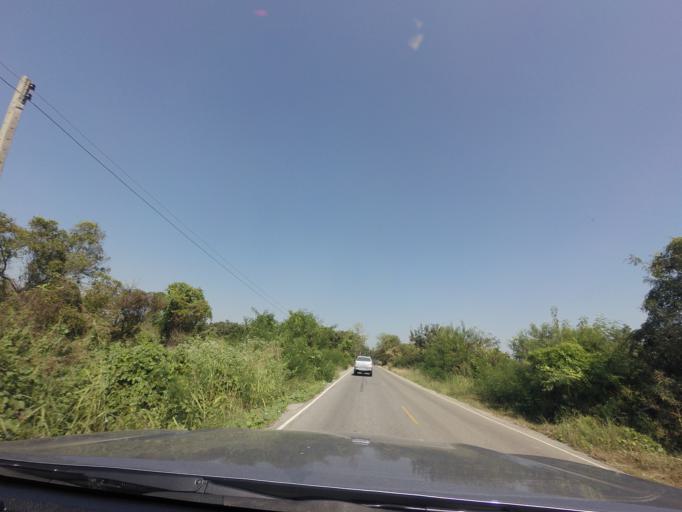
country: TH
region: Sukhothai
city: Si Samrong
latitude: 17.1250
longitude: 99.7815
